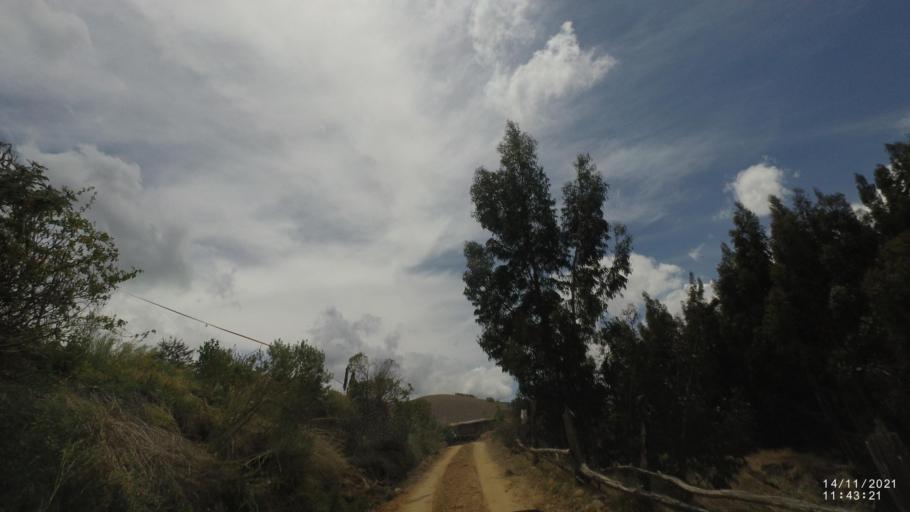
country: BO
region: Cochabamba
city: Colomi
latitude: -17.3520
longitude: -65.9917
